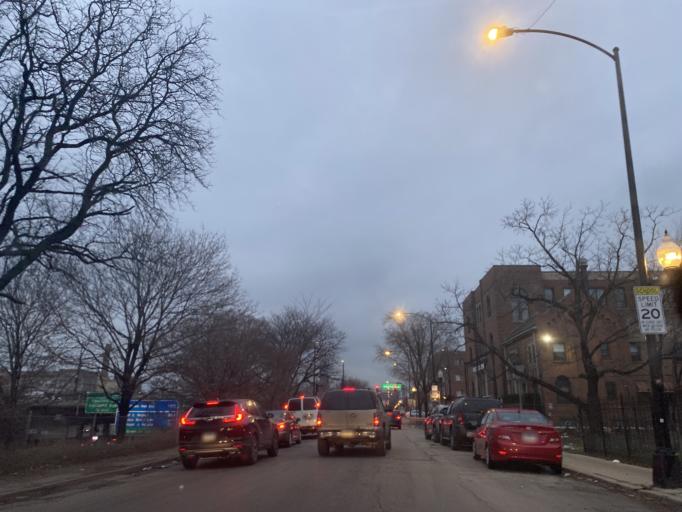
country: US
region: Illinois
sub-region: Cook County
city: Chicago
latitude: 41.8750
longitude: -87.6874
